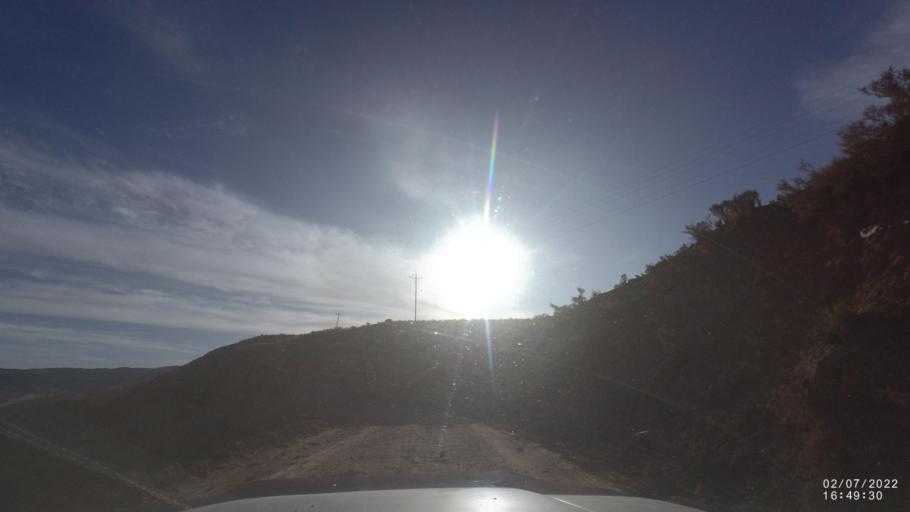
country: BO
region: Cochabamba
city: Irpa Irpa
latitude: -17.9742
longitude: -66.5266
